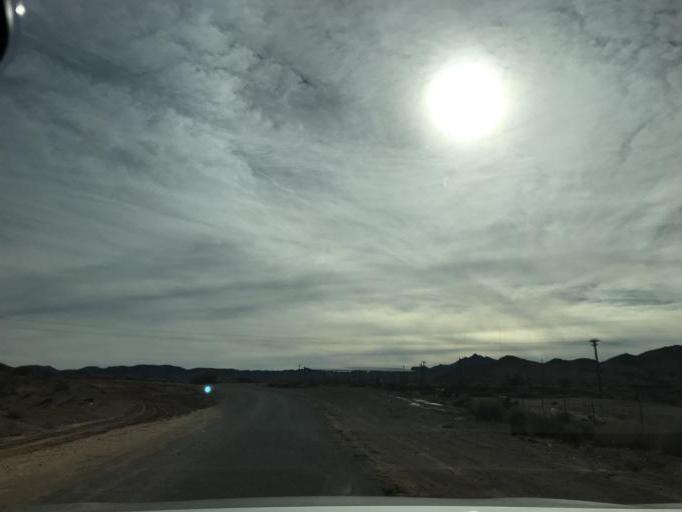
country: US
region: Nevada
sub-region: Clark County
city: Moapa Town
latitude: 36.6605
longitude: -114.5617
